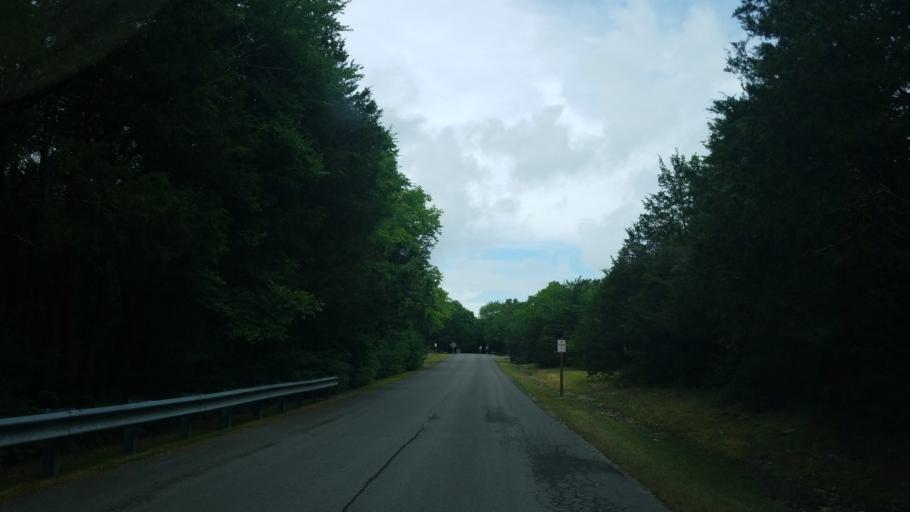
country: US
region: Tennessee
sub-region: Rutherford County
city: La Vergne
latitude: 36.1068
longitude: -86.5966
